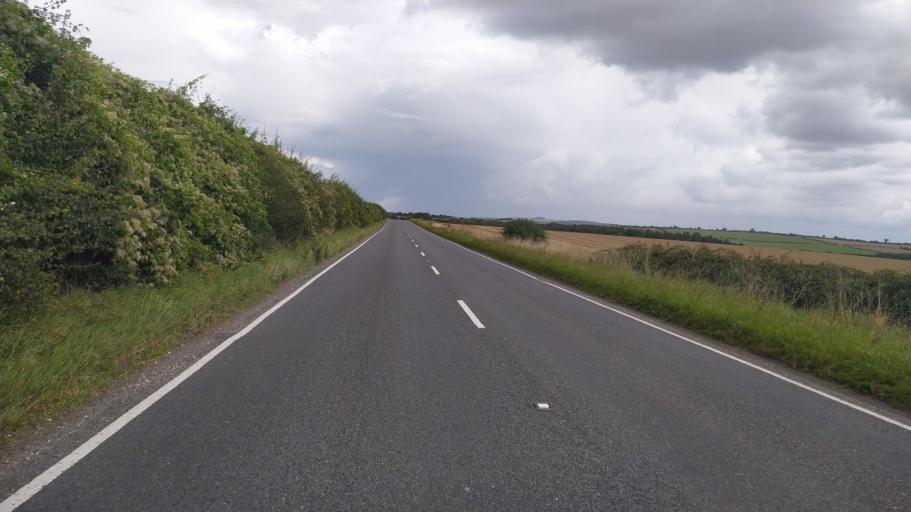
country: GB
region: England
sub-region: Dorset
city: Blandford Forum
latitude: 50.9039
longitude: -2.0745
